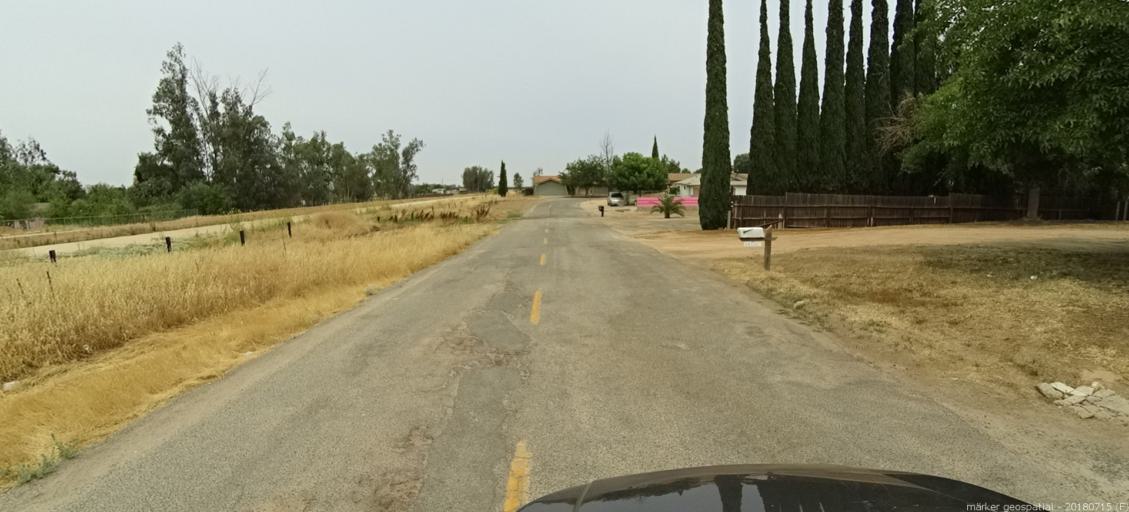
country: US
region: California
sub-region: Madera County
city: Madera Acres
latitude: 37.0216
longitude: -120.0820
